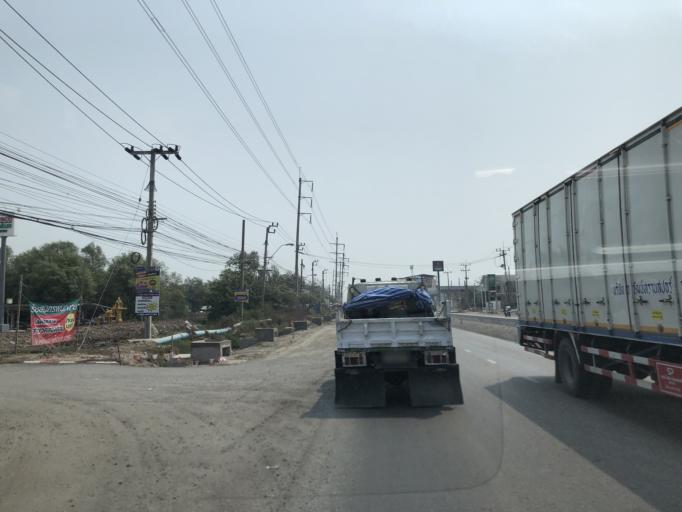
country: TH
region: Samut Prakan
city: Bang Bo
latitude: 13.5055
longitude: 100.8293
